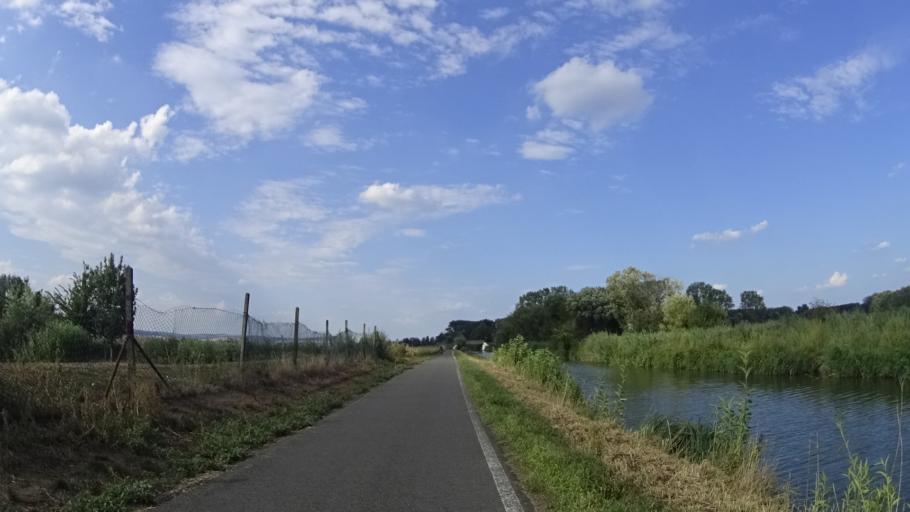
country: CZ
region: Zlin
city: Babice
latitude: 49.0995
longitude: 17.4746
